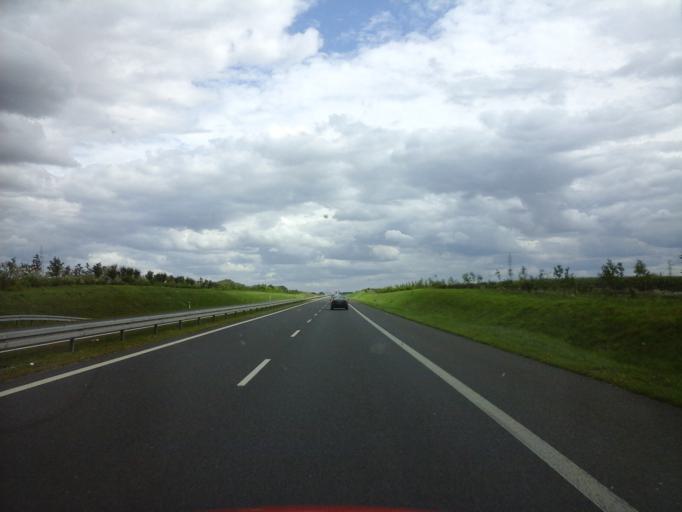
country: PL
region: West Pomeranian Voivodeship
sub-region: Powiat stargardzki
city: Stargard Szczecinski
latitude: 53.3113
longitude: 14.9985
